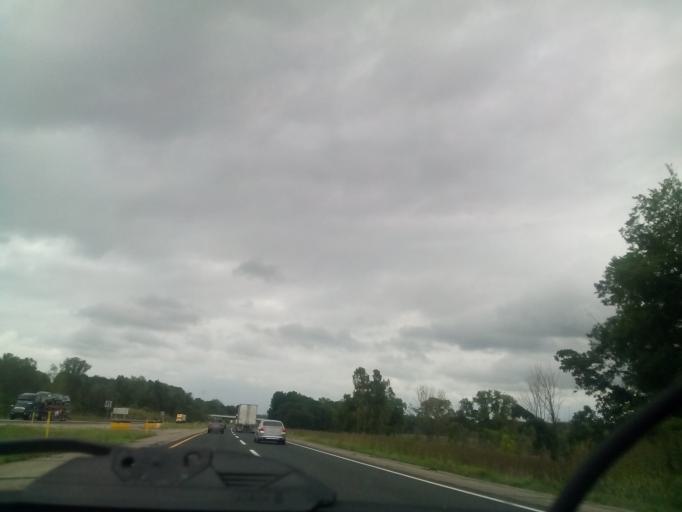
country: US
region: Indiana
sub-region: Steuben County
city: Fremont
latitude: 41.6433
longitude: -84.8356
